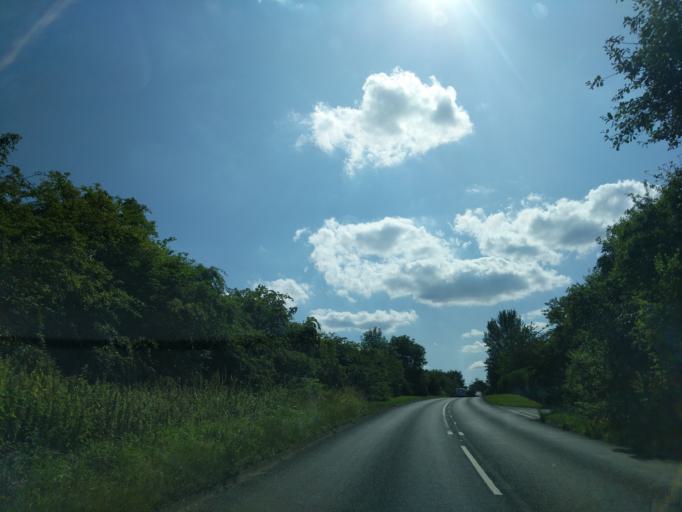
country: GB
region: England
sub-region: Staffordshire
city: Rugeley
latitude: 52.8078
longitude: -1.9235
